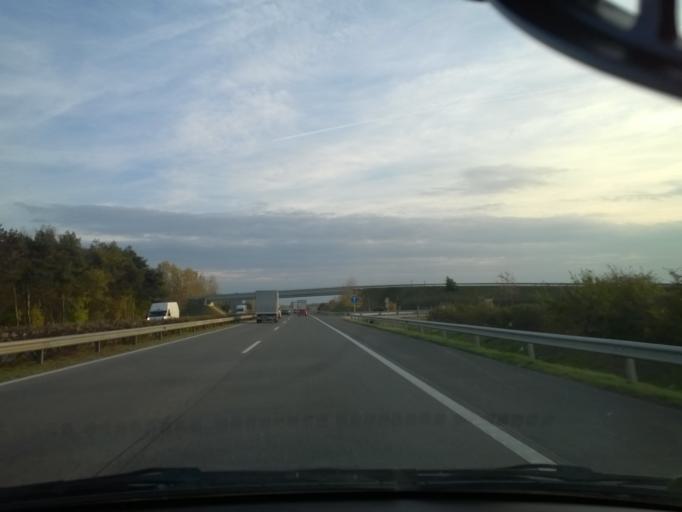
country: HU
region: Bacs-Kiskun
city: Lajosmizse
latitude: 46.9764
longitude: 19.6124
